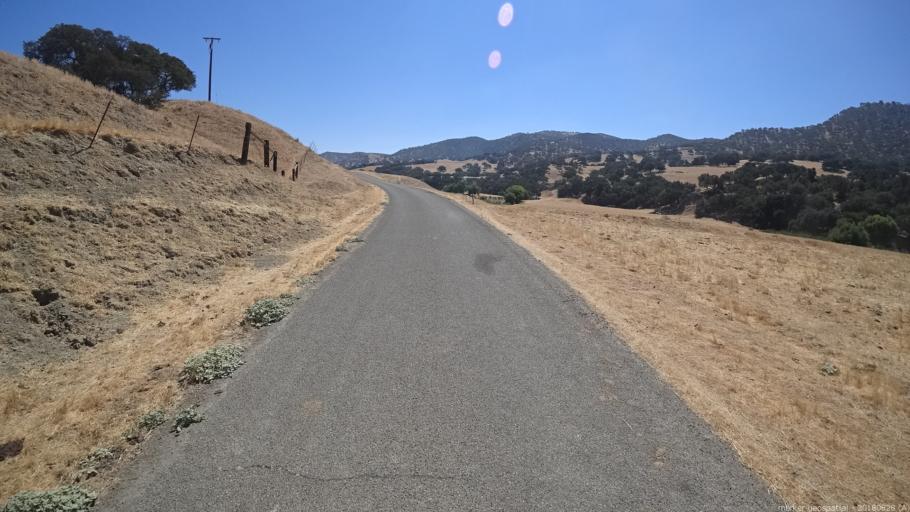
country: US
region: California
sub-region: San Luis Obispo County
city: San Miguel
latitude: 36.0665
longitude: -120.7695
